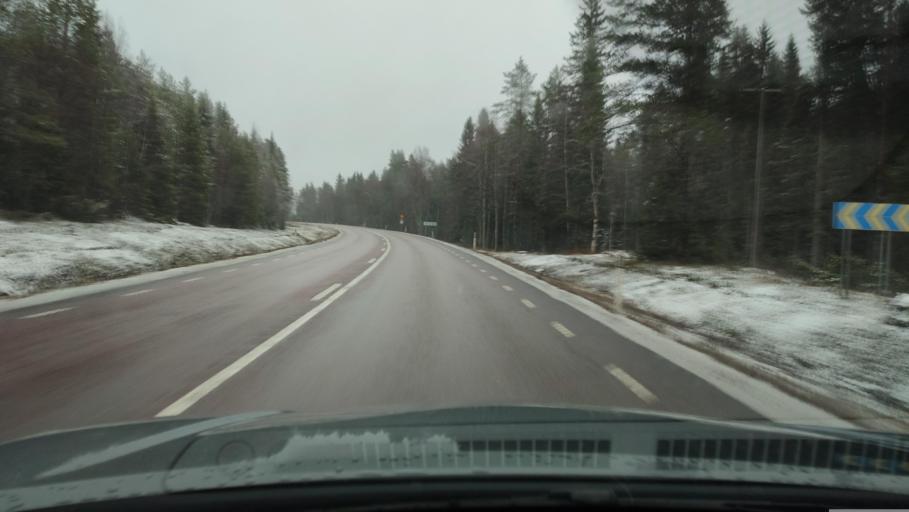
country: SE
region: Vaesterbotten
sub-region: Skelleftea Kommun
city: Burea
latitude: 64.3338
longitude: 21.2619
